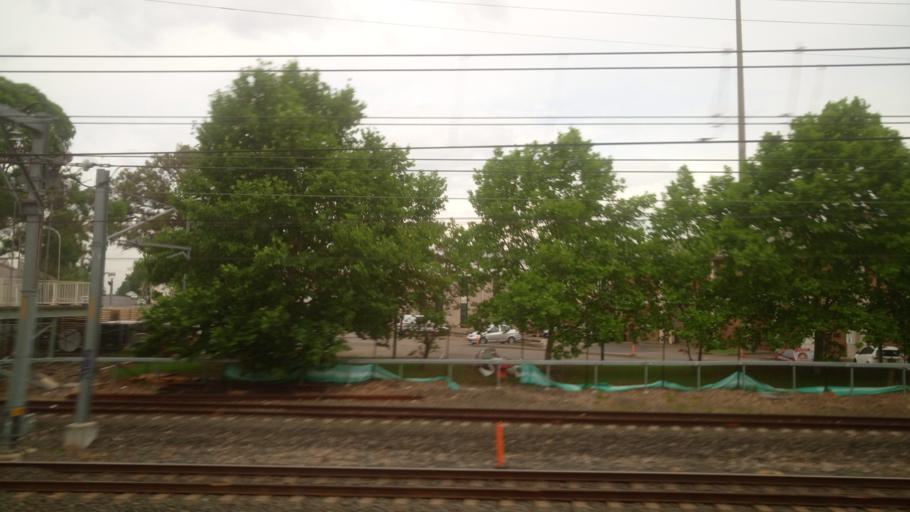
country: AU
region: New South Wales
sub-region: Parramatta
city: Granville
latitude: -33.8356
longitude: 151.0163
